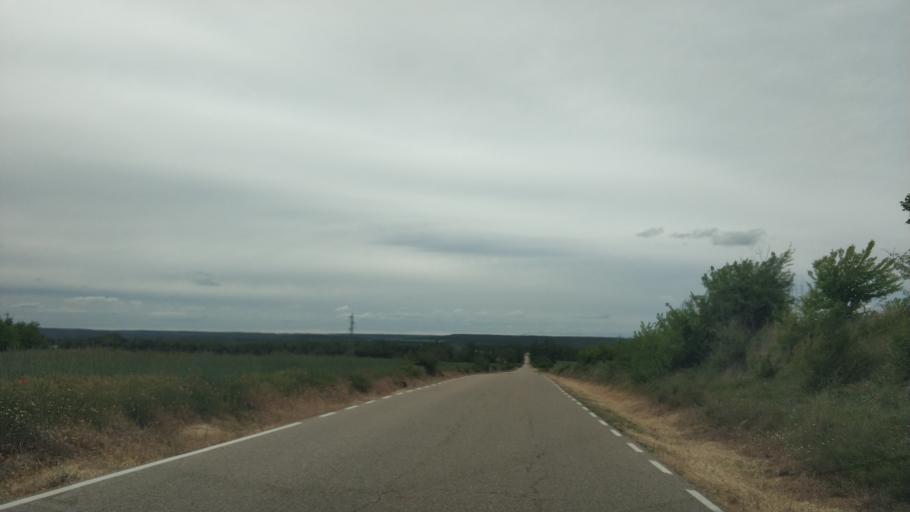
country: ES
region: Castille and Leon
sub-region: Provincia de Soria
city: Berlanga de Duero
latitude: 41.4816
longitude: -2.8646
